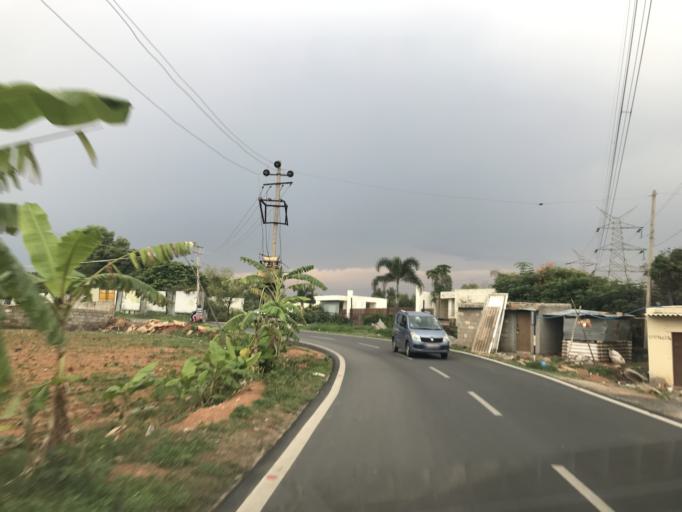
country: IN
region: Karnataka
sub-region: Bangalore Rural
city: Devanhalli
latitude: 13.1781
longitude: 77.6496
